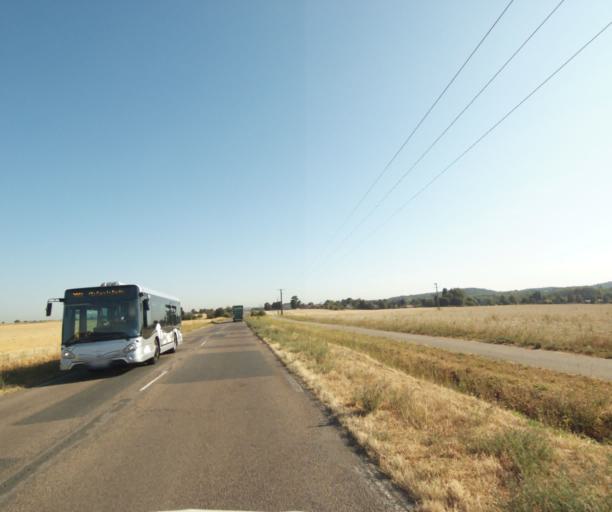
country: FR
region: Ile-de-France
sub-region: Departement de l'Essonne
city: Baulne
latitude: 48.5047
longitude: 2.3537
